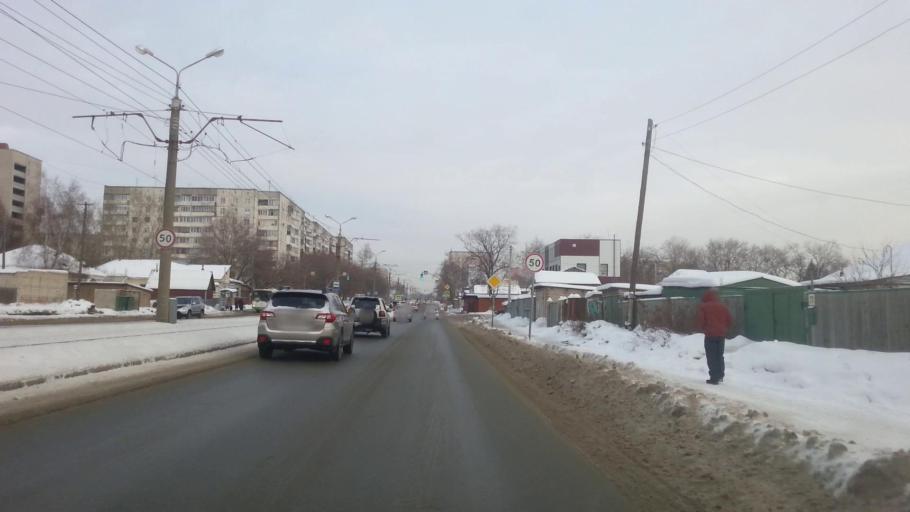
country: RU
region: Altai Krai
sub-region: Gorod Barnaulskiy
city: Barnaul
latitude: 53.3681
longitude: 83.7367
